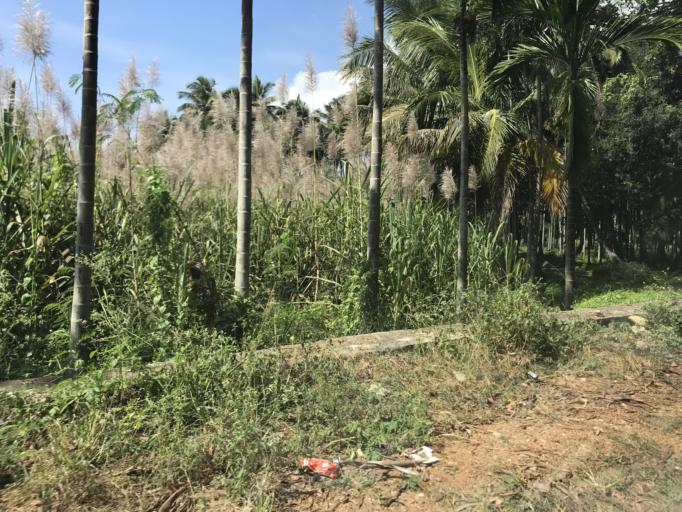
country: IN
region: Karnataka
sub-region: Mandya
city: Shrirangapattana
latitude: 12.4218
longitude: 76.6572
